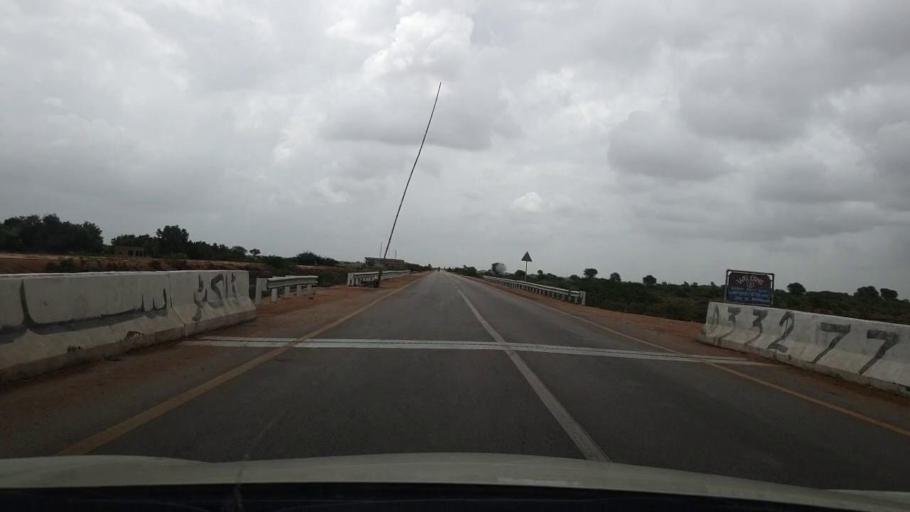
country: PK
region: Sindh
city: Mirpur Batoro
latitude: 24.6378
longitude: 68.3859
